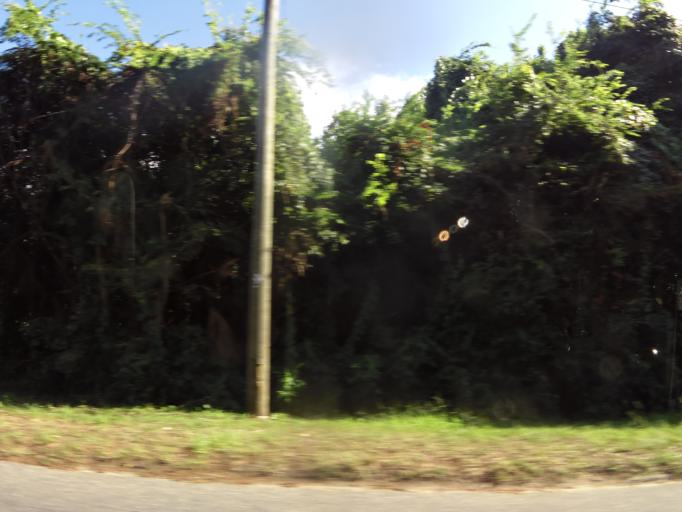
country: US
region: Florida
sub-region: Nassau County
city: Fernandina Beach
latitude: 30.6622
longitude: -81.4626
